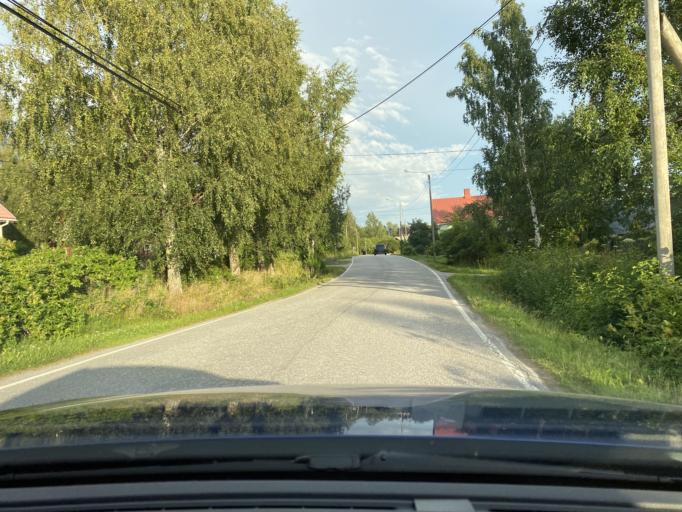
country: FI
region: Ostrobothnia
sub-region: Vaasa
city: Korsnaes
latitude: 62.9714
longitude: 21.1834
